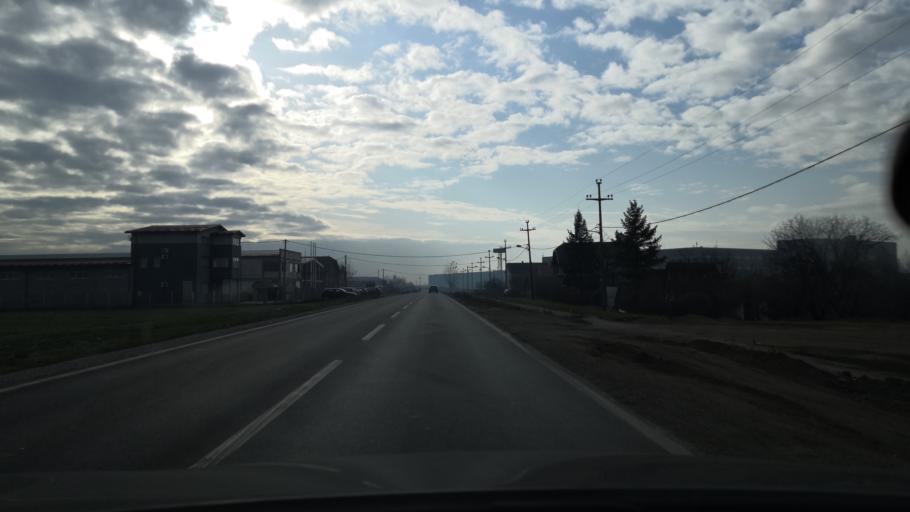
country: RS
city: Ugrinovci
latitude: 44.8576
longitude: 20.2051
